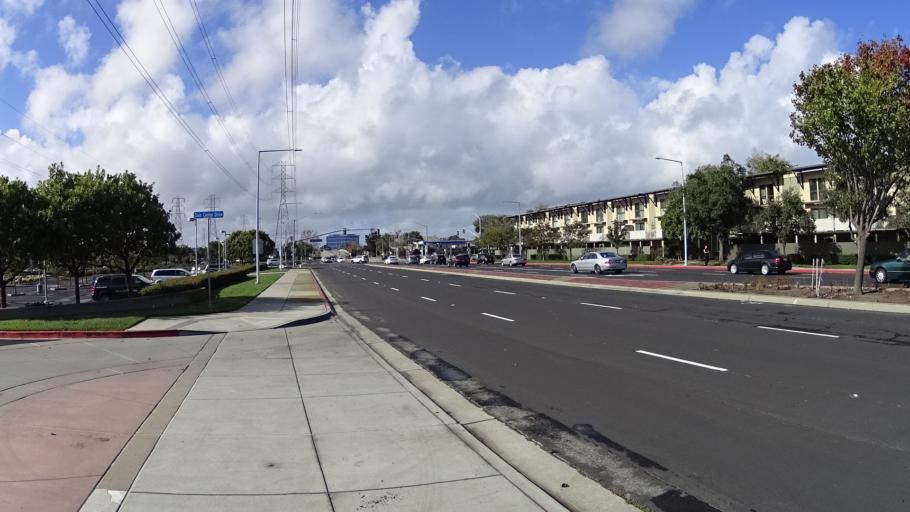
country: US
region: California
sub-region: San Mateo County
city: Foster City
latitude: 37.5606
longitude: -122.2680
